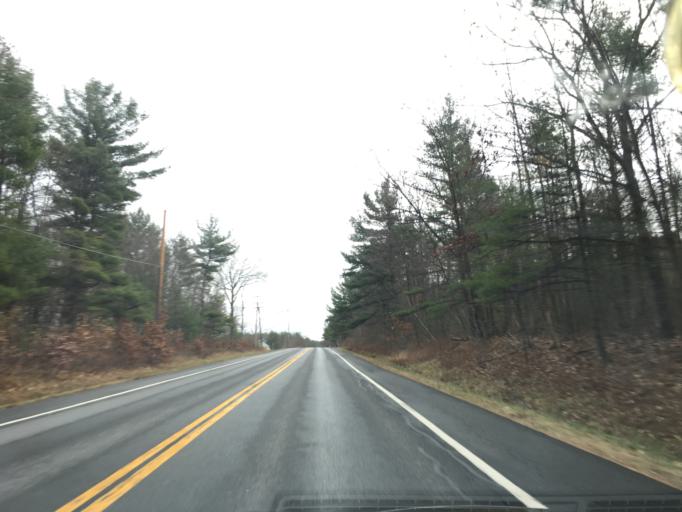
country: US
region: New York
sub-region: Rensselaer County
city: Averill Park
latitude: 42.6506
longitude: -73.5581
